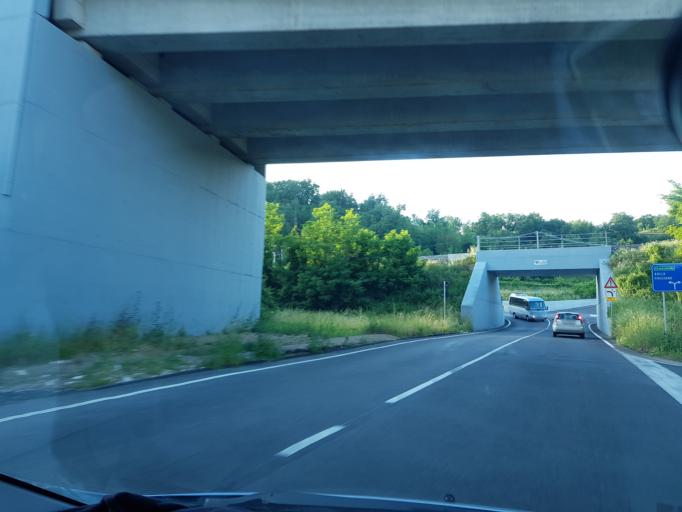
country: IT
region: Tuscany
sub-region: Provincia di Massa-Carrara
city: Fivizzano
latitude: 44.2016
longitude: 10.0885
